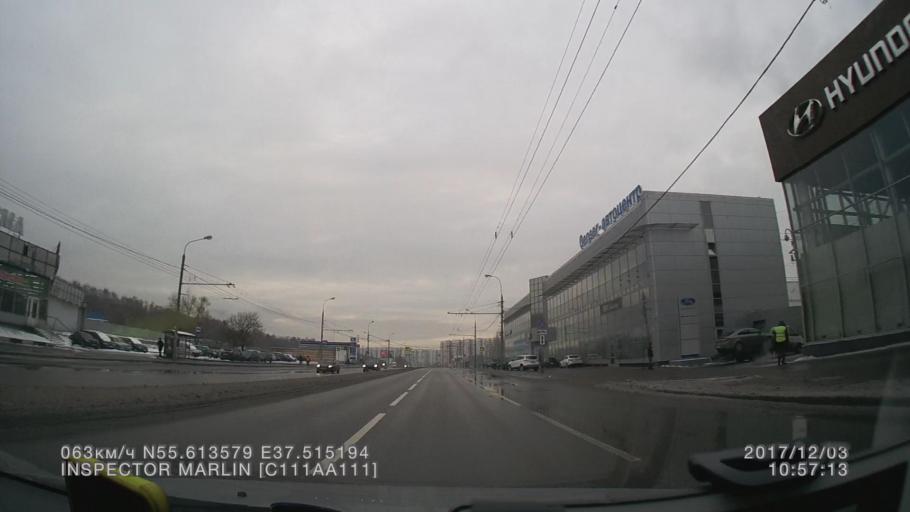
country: RU
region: Moscow
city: Yasenevo
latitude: 55.6134
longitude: 37.5154
